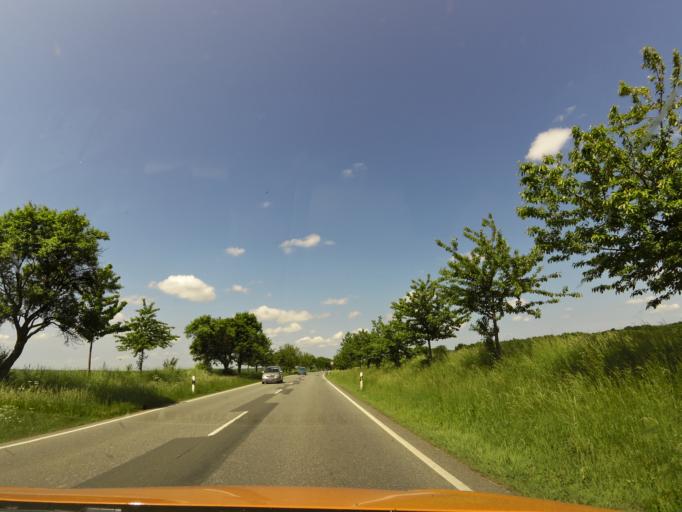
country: DE
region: Mecklenburg-Vorpommern
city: Lutzow
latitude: 53.6757
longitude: 11.1454
